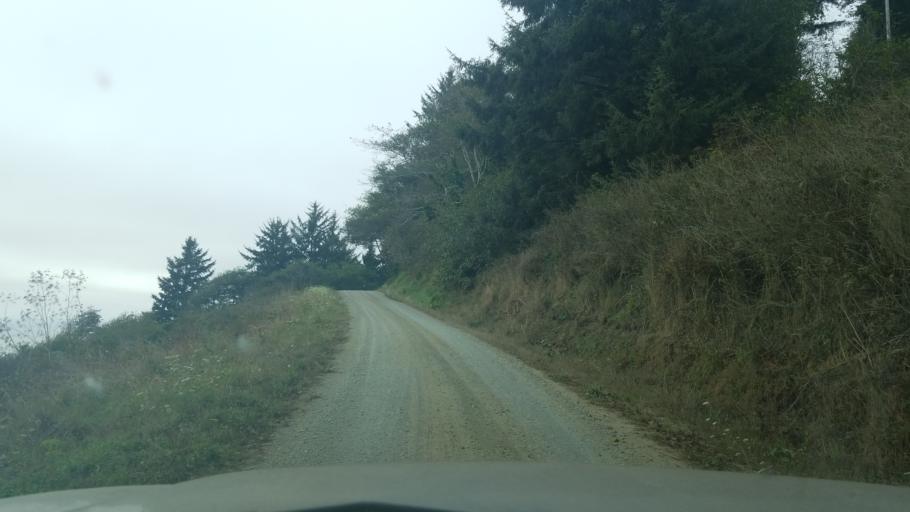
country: US
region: California
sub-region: Del Norte County
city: Bertsch-Oceanview
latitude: 41.5235
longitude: -124.0788
